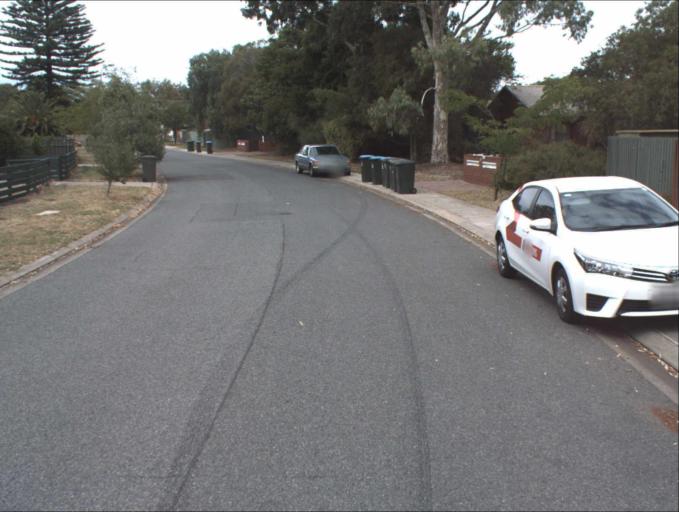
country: AU
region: South Australia
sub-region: Port Adelaide Enfield
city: Birkenhead
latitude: -34.8108
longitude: 138.4984
